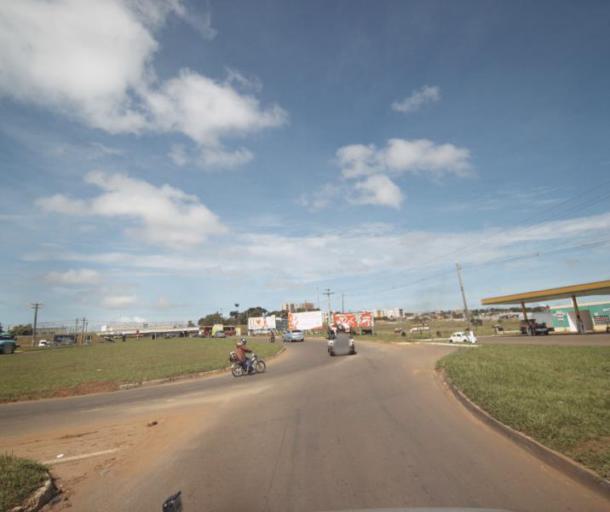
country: BR
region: Goias
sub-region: Anapolis
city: Anapolis
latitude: -16.2848
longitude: -48.9434
